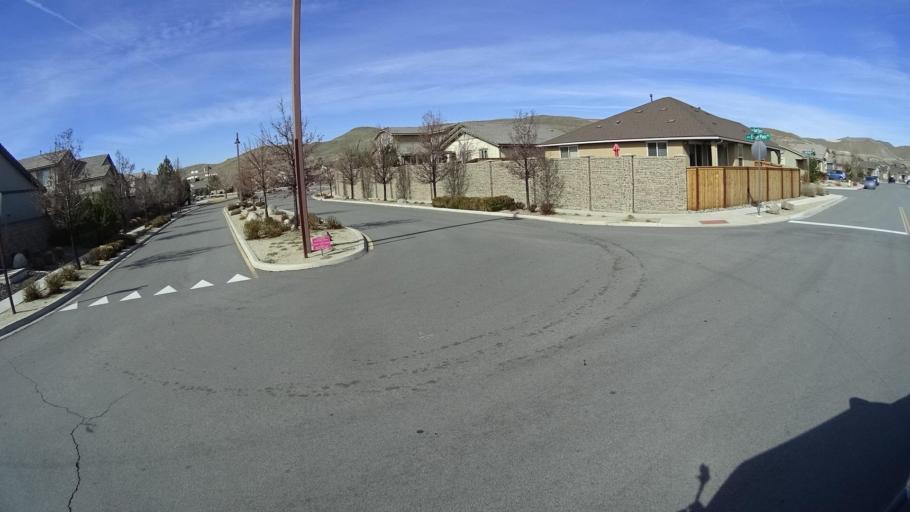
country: US
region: Nevada
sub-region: Washoe County
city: Sun Valley
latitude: 39.6009
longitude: -119.7274
